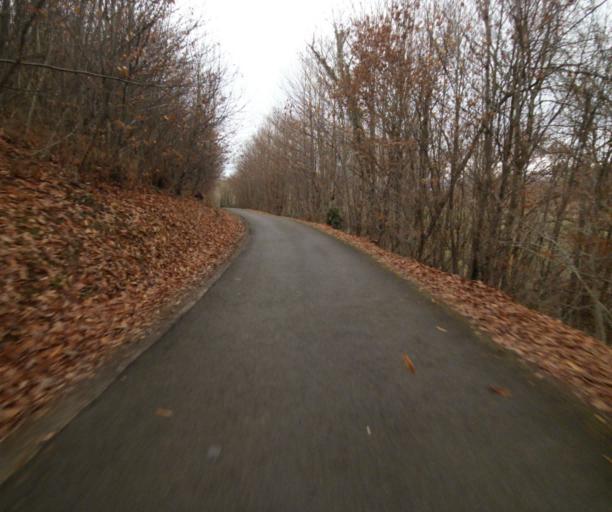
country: FR
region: Limousin
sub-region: Departement de la Correze
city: Chameyrat
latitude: 45.2291
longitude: 1.6870
